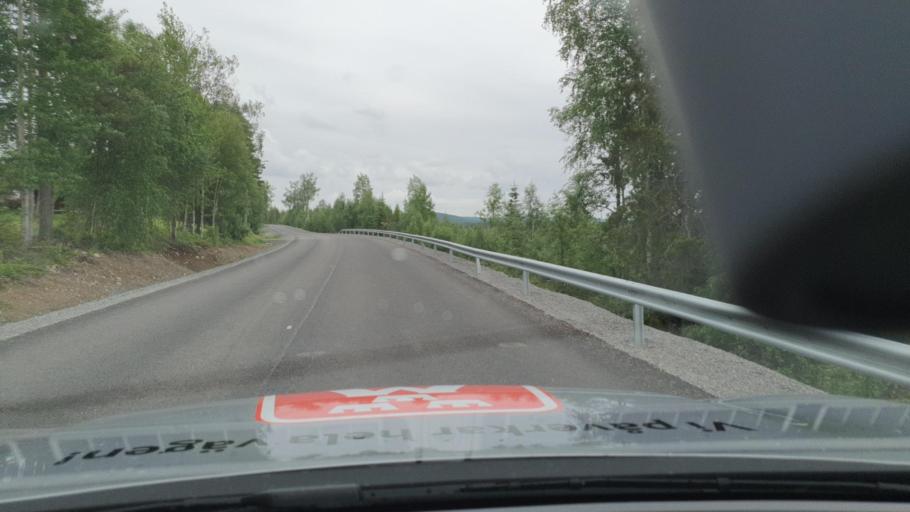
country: SE
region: Norrbotten
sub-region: Overtornea Kommun
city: OEvertornea
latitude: 66.5941
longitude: 23.3112
